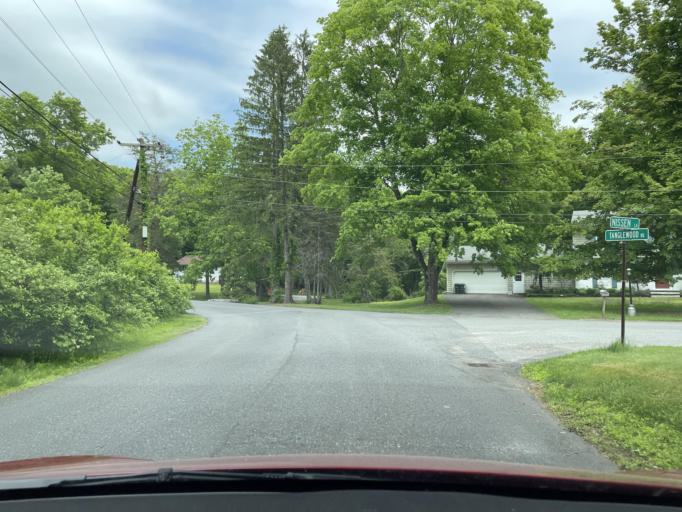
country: US
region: New York
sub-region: Ulster County
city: West Hurley
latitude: 42.0137
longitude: -74.0983
